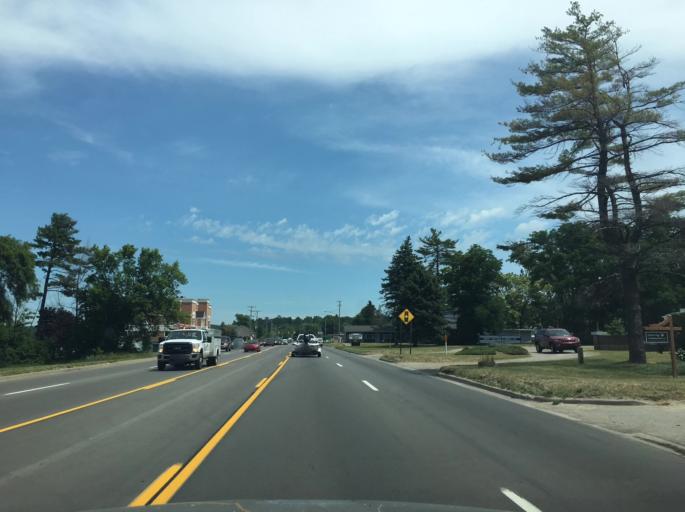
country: US
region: Michigan
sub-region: Grand Traverse County
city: Traverse City
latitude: 44.7630
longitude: -85.5096
